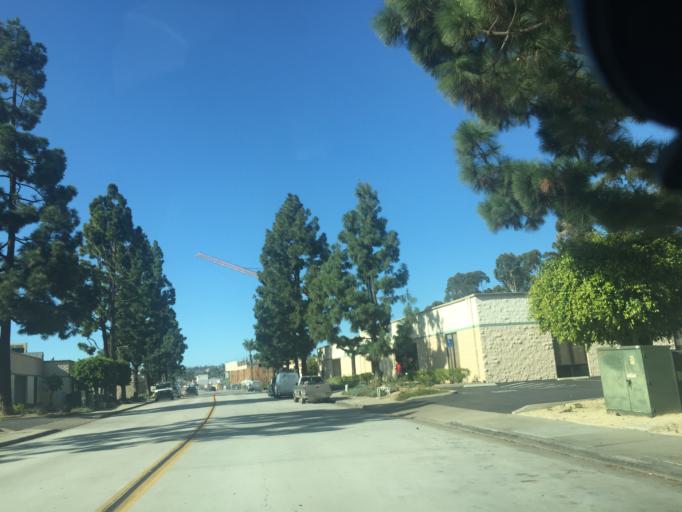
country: US
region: California
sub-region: San Diego County
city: La Mesa
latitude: 32.7827
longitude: -117.0931
